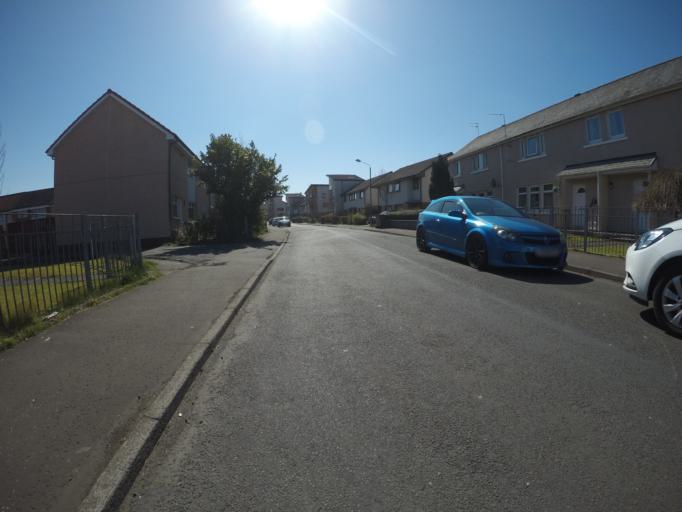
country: GB
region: Scotland
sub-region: North Ayrshire
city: Irvine
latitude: 55.6235
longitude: -4.6654
